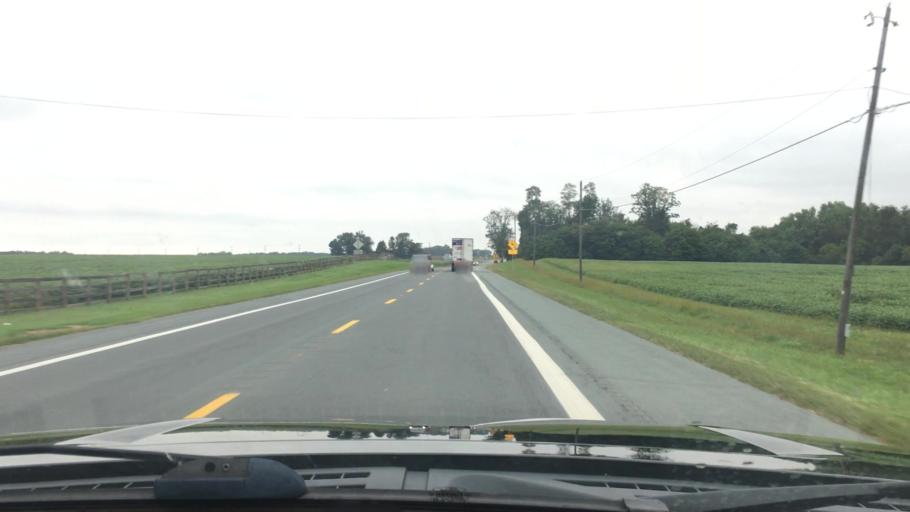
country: US
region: Maryland
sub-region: Cecil County
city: Elkton
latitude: 39.4806
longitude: -75.8481
